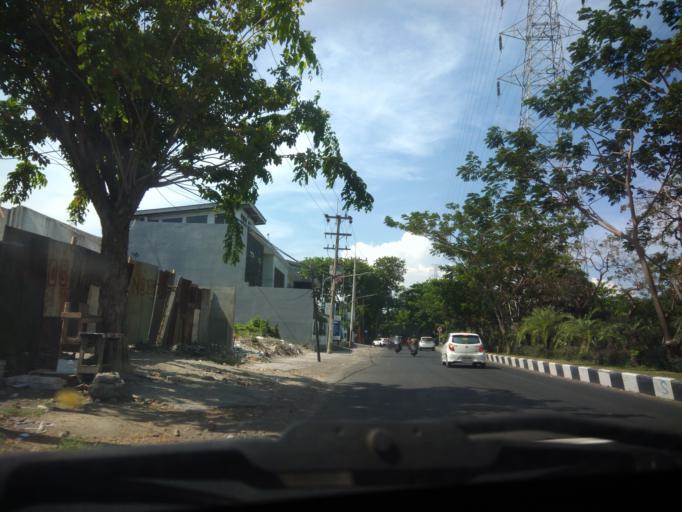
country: ID
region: East Java
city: Mulyorejo
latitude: -7.2696
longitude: 112.7738
